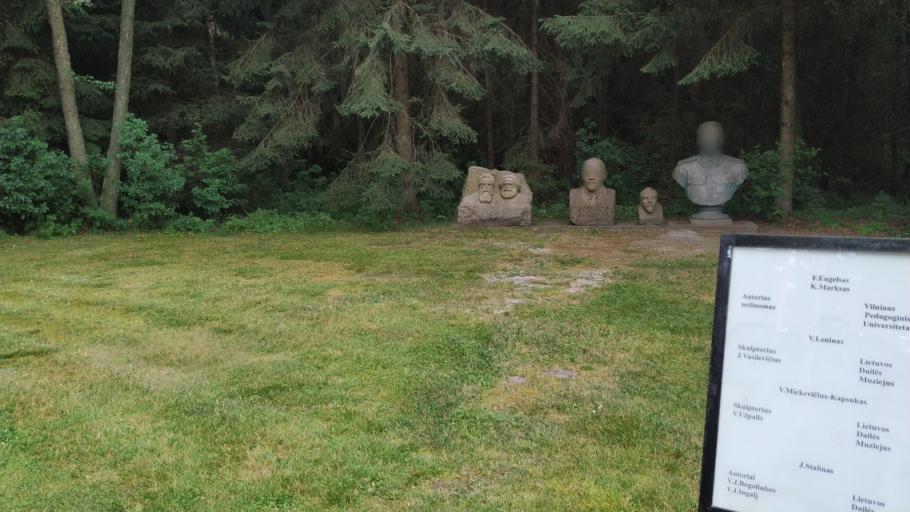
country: LT
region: Alytaus apskritis
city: Druskininkai
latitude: 54.0205
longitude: 24.0773
